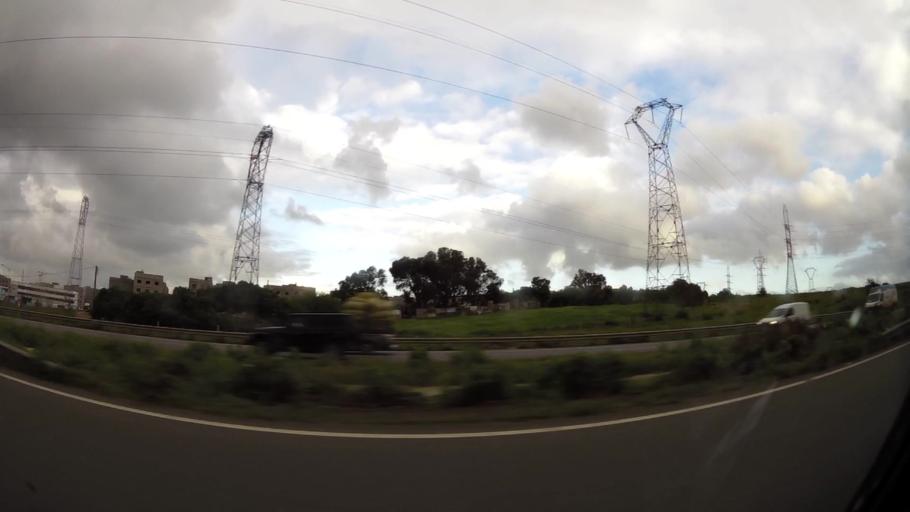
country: MA
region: Grand Casablanca
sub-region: Mohammedia
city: Mohammedia
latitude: 33.6336
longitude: -7.4233
